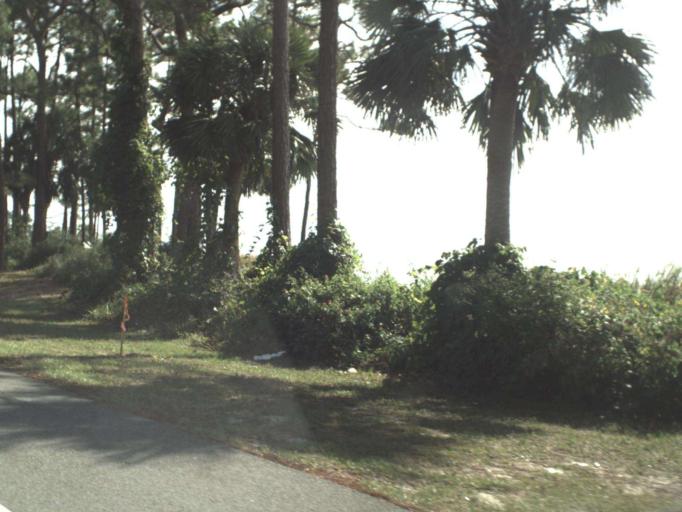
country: US
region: Florida
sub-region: Gulf County
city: Port Saint Joe
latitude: 29.8009
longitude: -85.3012
